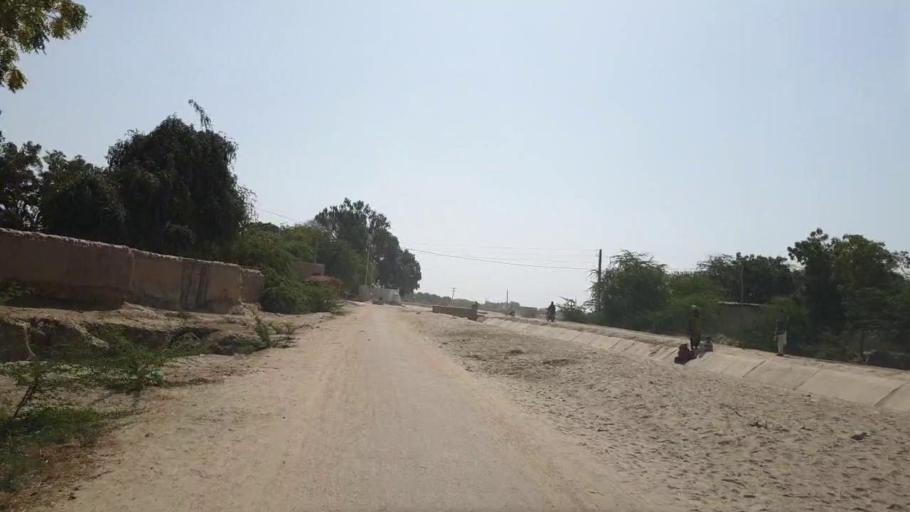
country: PK
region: Sindh
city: Naukot
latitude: 24.9754
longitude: 69.4818
